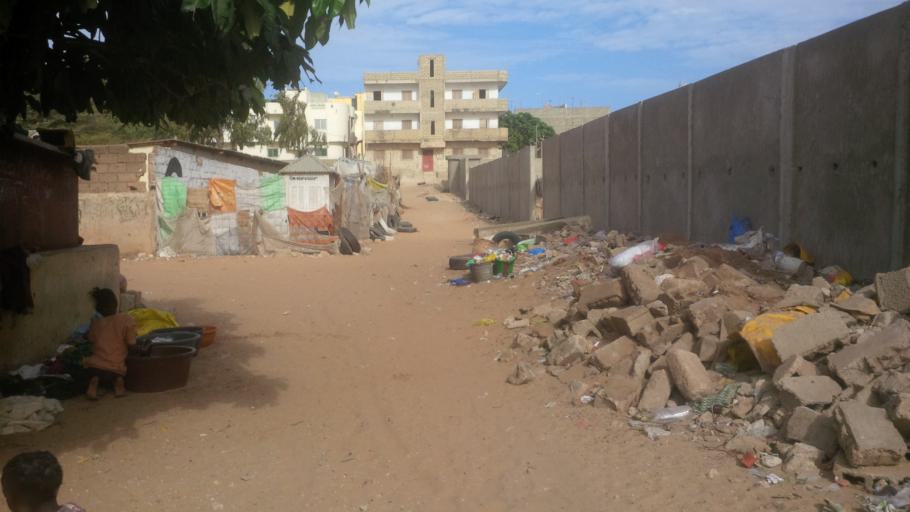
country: SN
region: Dakar
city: Pikine
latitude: 14.7809
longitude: -17.3784
